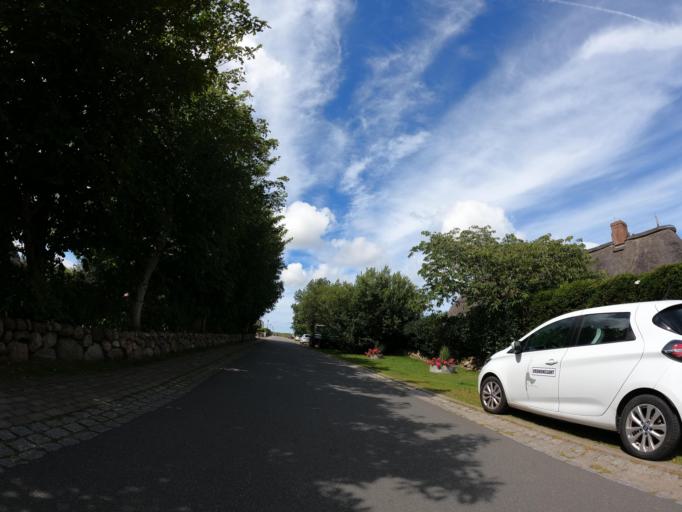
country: DE
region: Schleswig-Holstein
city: Sylt-Ost
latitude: 54.8744
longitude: 8.4269
